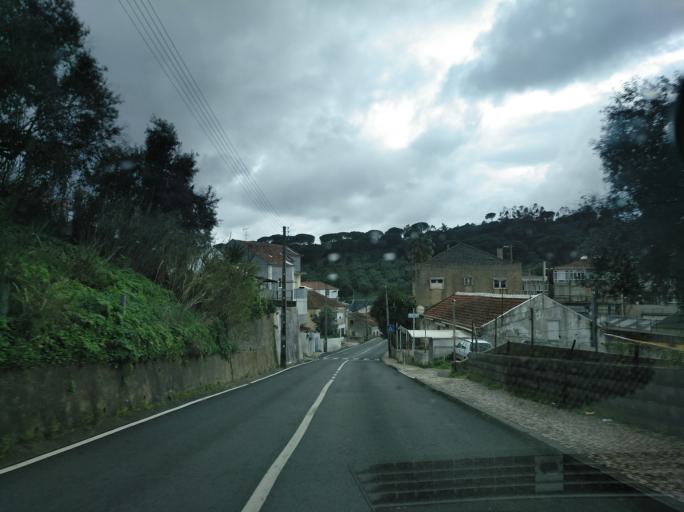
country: PT
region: Lisbon
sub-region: Odivelas
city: Famoes
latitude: 38.7819
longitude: -9.2076
